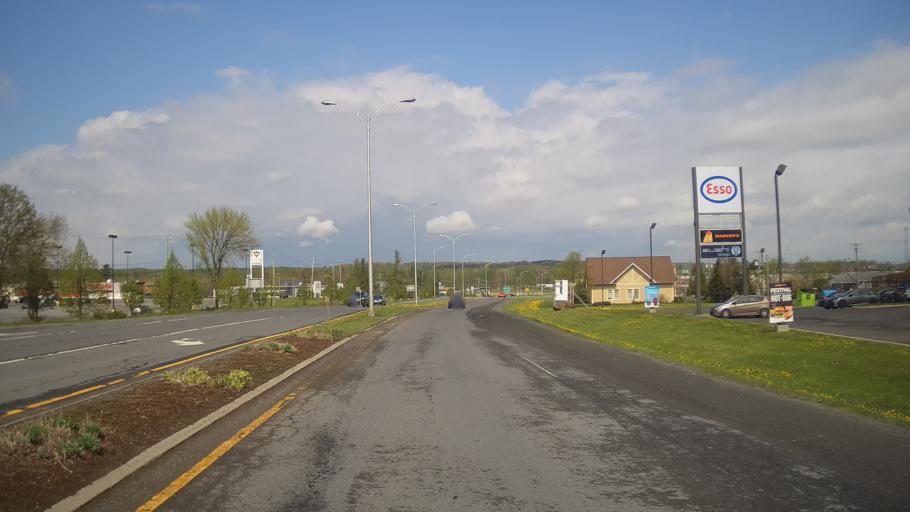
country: CA
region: Quebec
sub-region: Monteregie
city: Cowansville
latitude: 45.1907
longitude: -72.7557
